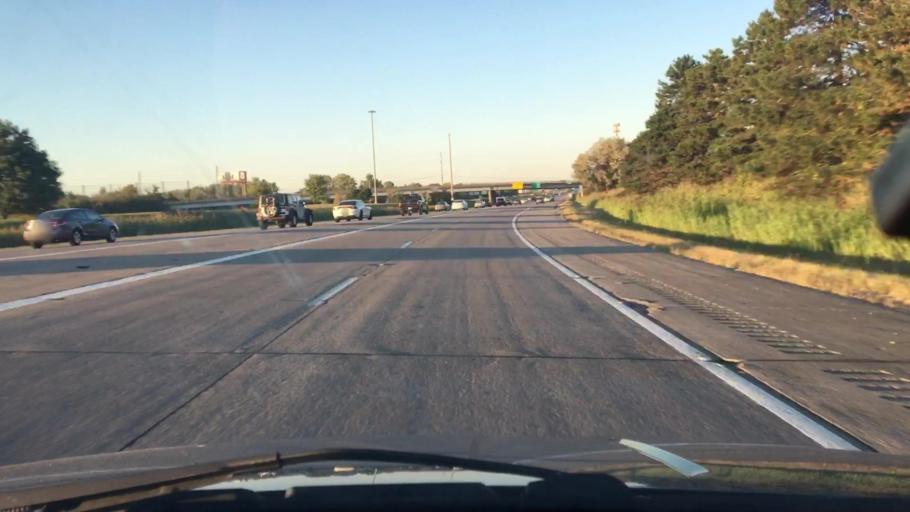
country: US
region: Michigan
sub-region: Wayne County
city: Plymouth
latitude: 42.3929
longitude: -83.4327
